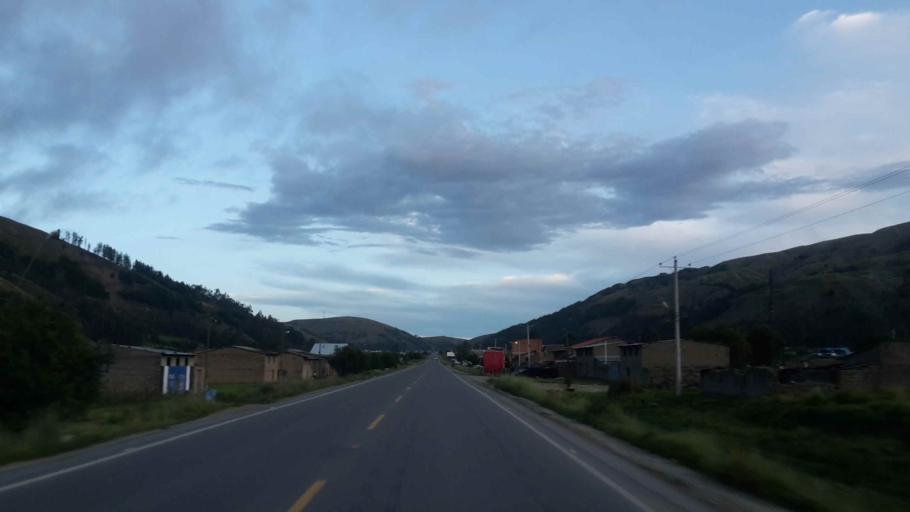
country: BO
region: Cochabamba
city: Colomi
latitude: -17.3450
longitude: -65.8586
